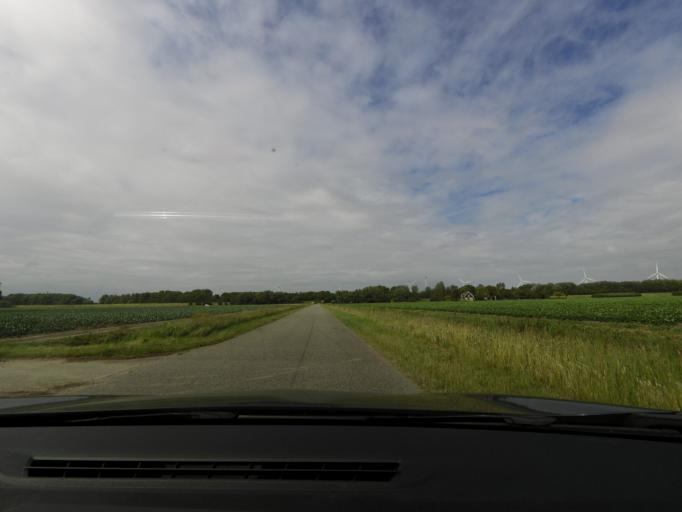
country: NL
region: South Holland
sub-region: Gemeente Brielle
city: Brielle
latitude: 51.9178
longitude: 4.1503
